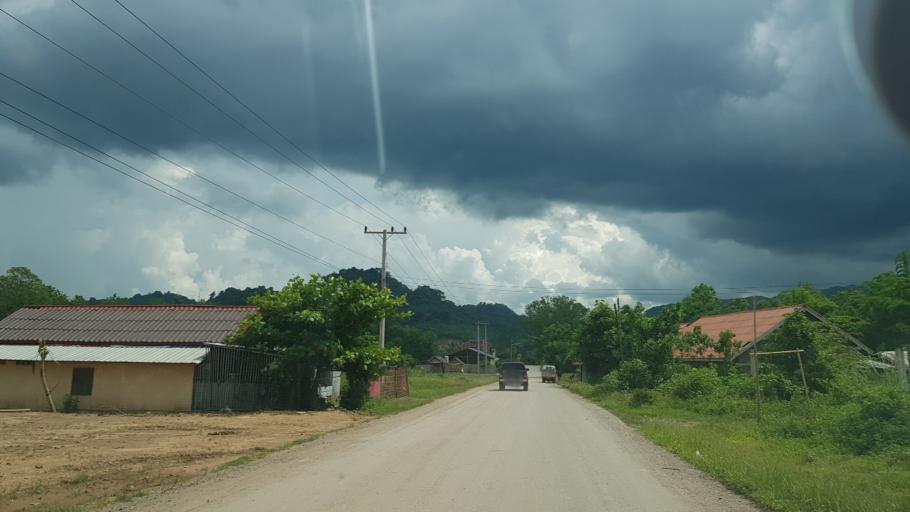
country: LA
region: Oudomxai
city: Muang Xay
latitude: 20.6763
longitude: 101.9696
